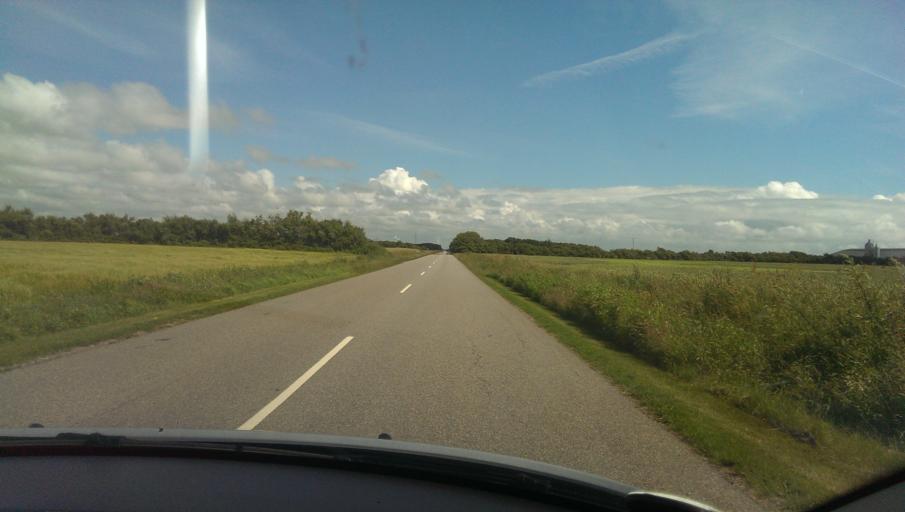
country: DK
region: Central Jutland
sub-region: Ringkobing-Skjern Kommune
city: Ringkobing
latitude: 56.1368
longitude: 8.1648
